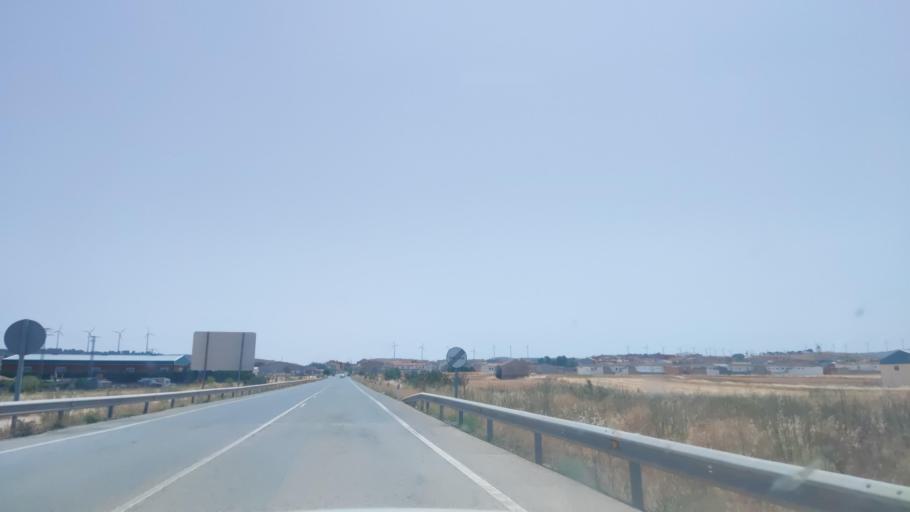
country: ES
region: Castille-La Mancha
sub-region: Provincia de Albacete
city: Pozo-Canada
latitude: 38.8100
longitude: -1.7383
